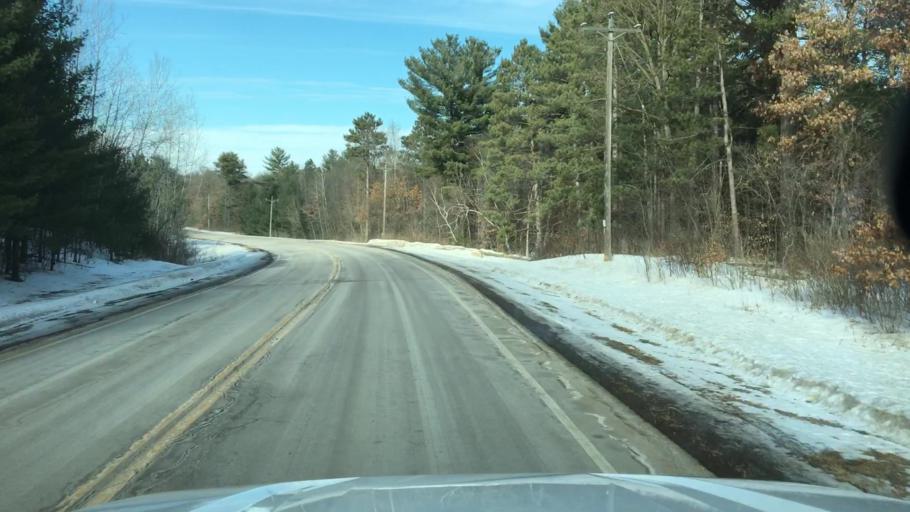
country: US
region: Wisconsin
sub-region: Polk County
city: Saint Croix Falls
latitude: 45.4579
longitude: -92.6744
